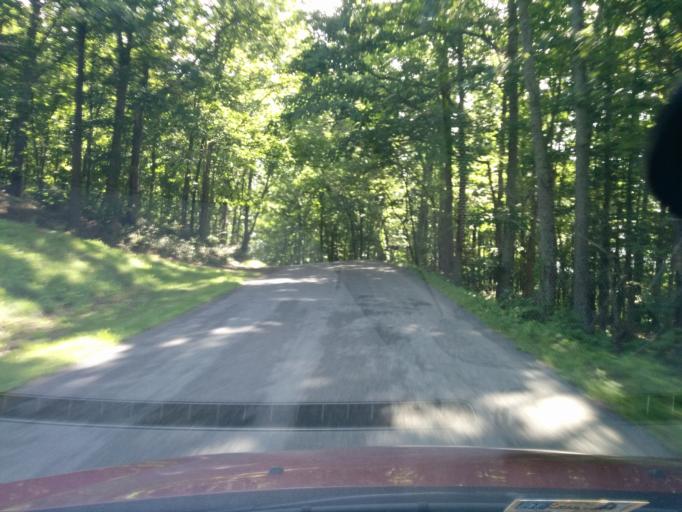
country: US
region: Virginia
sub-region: City of Lexington
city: Lexington
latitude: 37.7723
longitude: -79.4881
